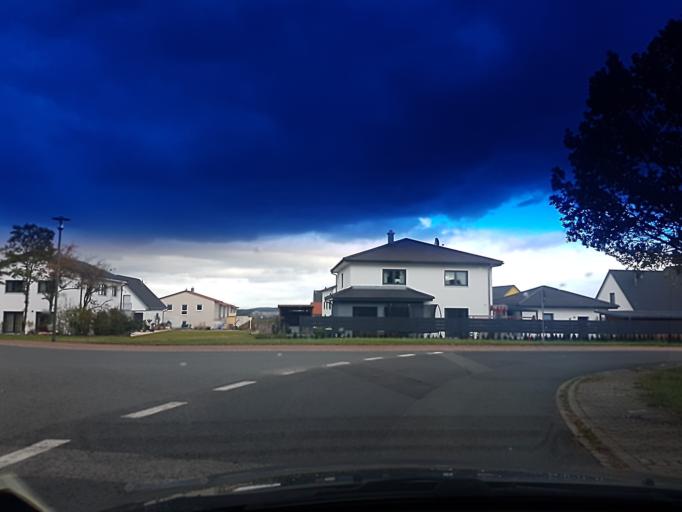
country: DE
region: Bavaria
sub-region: Regierungsbezirk Mittelfranken
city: Burghaslach
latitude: 49.7384
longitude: 10.6051
